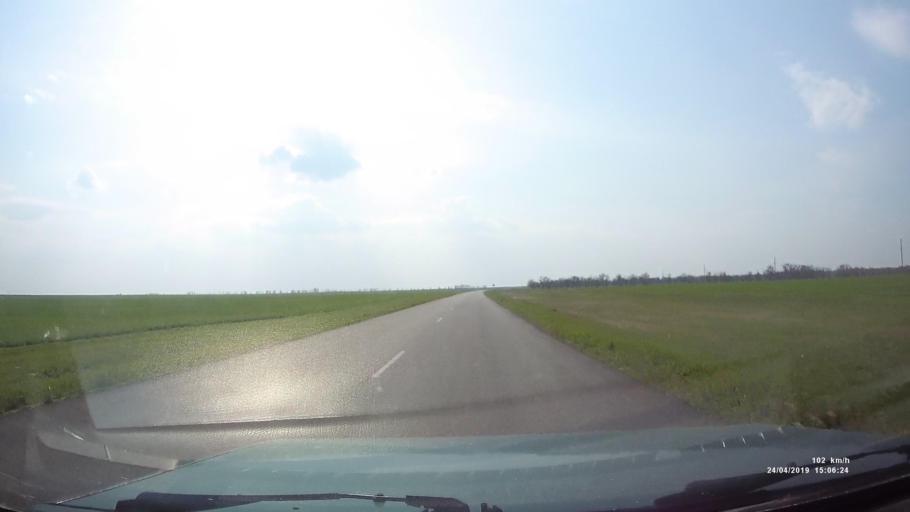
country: RU
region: Rostov
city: Remontnoye
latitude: 46.5589
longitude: 43.4278
